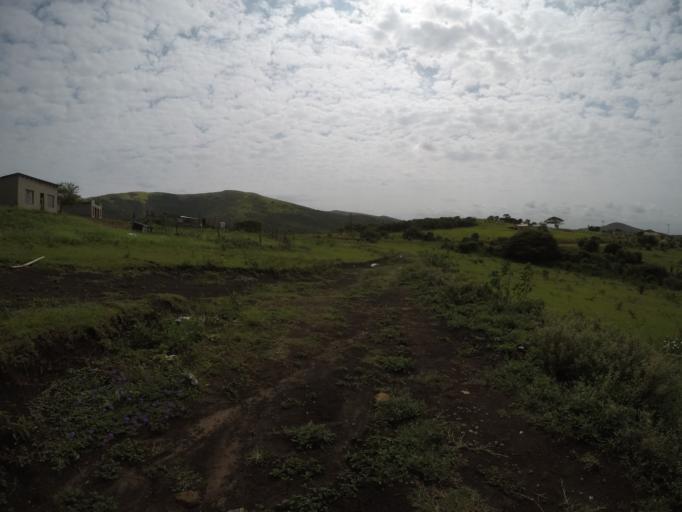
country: ZA
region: KwaZulu-Natal
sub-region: uThungulu District Municipality
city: Empangeni
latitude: -28.6168
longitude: 31.9003
